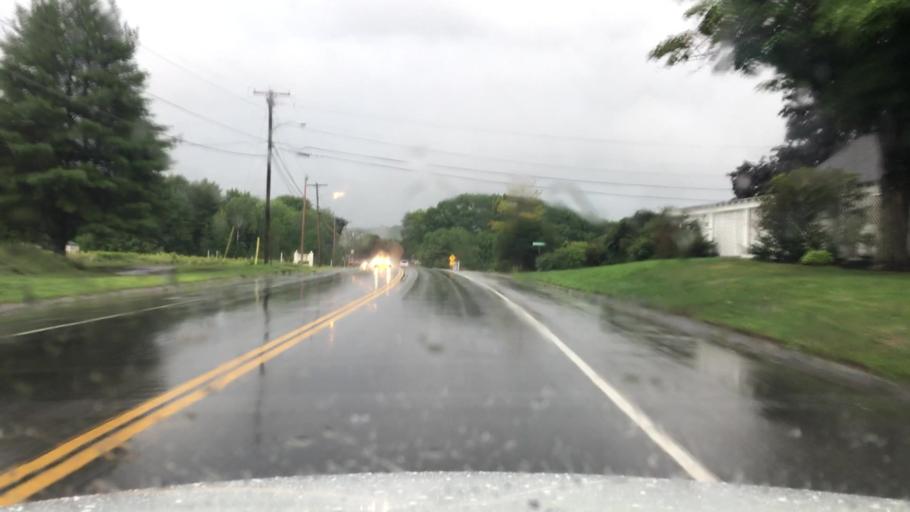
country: US
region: Maine
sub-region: Kennebec County
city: Manchester
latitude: 44.3241
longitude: -69.8775
